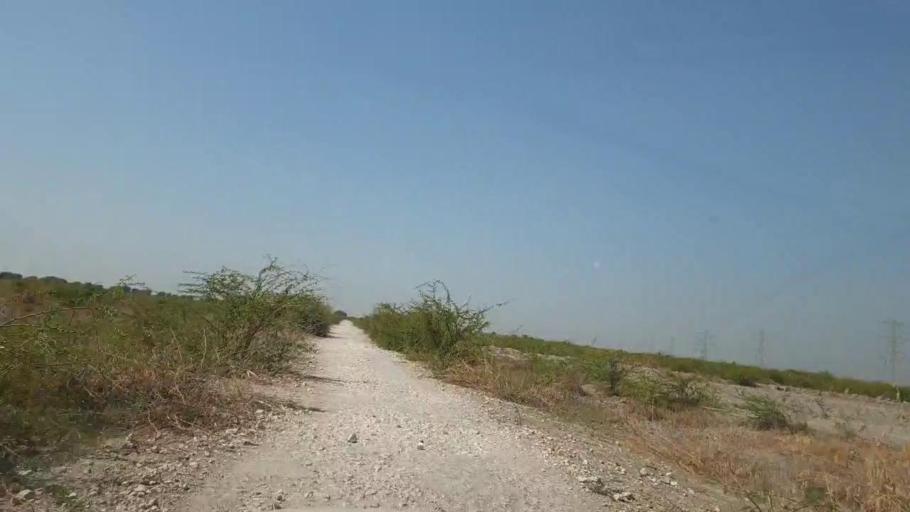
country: PK
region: Sindh
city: Kunri
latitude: 25.0965
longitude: 69.4761
